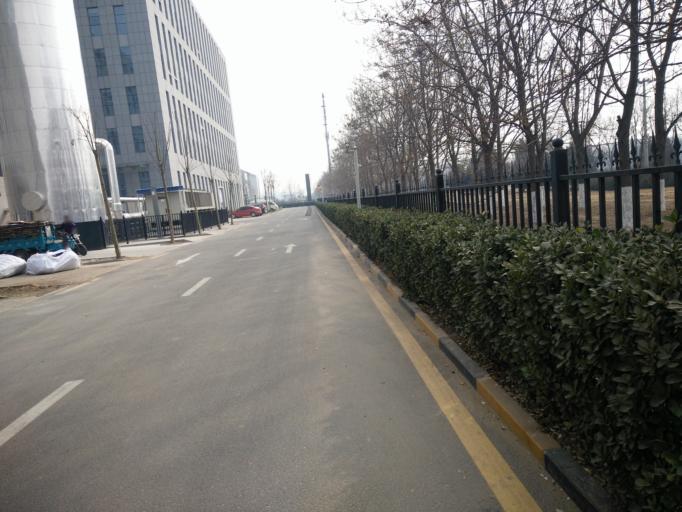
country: CN
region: Beijing
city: Jiugong
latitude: 39.7593
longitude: 116.5094
